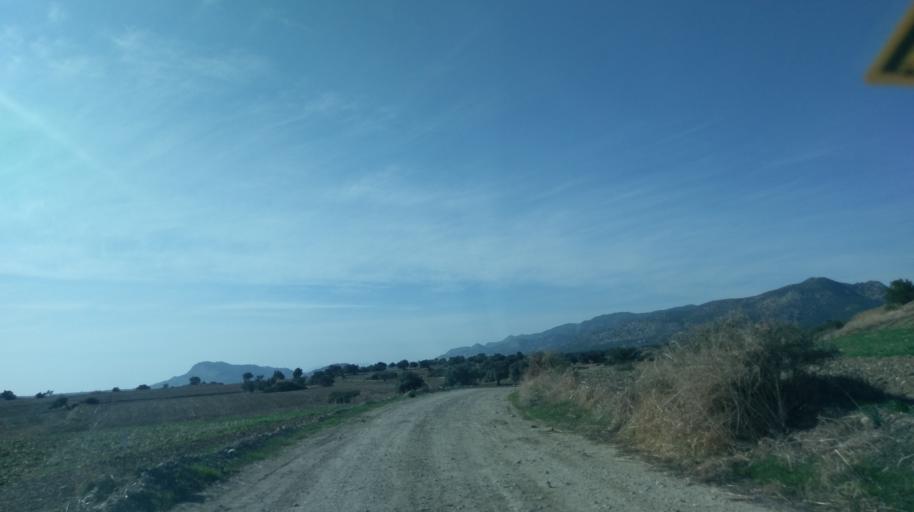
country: CY
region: Ammochostos
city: Trikomo
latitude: 35.3409
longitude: 33.8610
